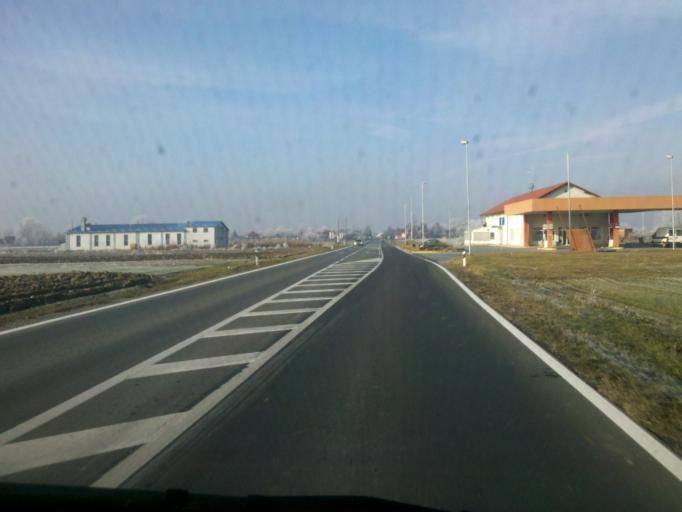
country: HR
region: Virovitick-Podravska
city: Pitomaca
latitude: 45.9750
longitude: 17.1716
